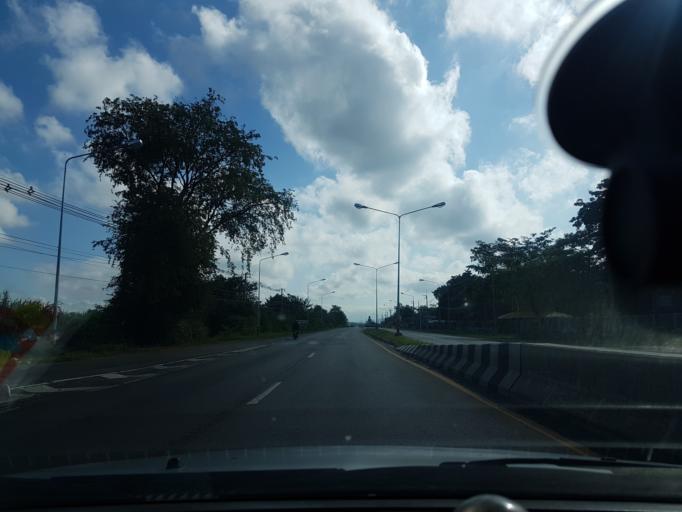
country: TH
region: Lop Buri
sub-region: Amphoe Tha Luang
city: Tha Luang
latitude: 15.0791
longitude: 101.0192
